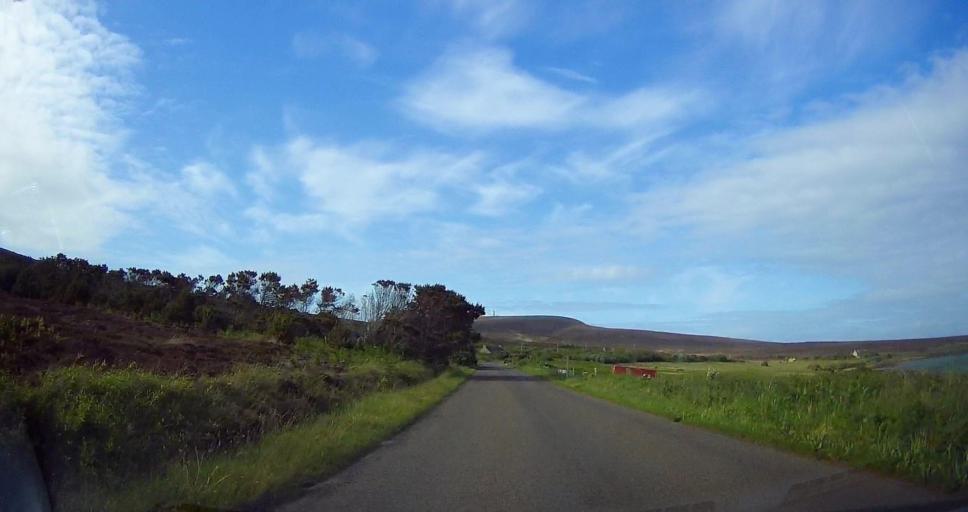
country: GB
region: Scotland
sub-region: Orkney Islands
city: Stromness
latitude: 58.7970
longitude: -3.2527
